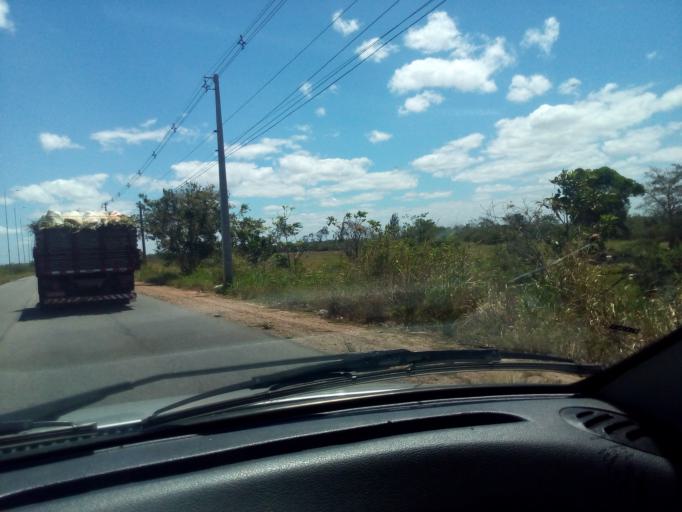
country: BR
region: Rio Grande do Norte
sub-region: Sao Goncalo Do Amarante
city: Sao Goncalo do Amarante
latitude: -5.8024
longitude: -35.3290
